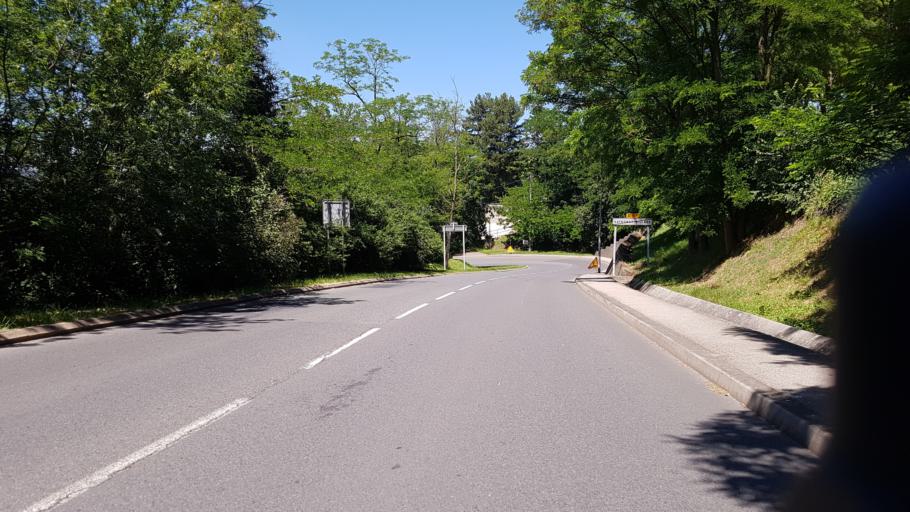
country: FR
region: Rhone-Alpes
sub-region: Departement du Rhone
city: Sathonay-Village
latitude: 45.8308
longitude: 4.8788
